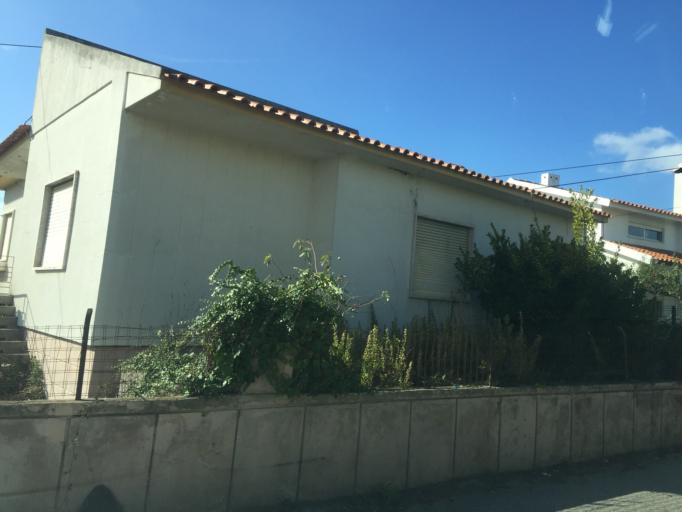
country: PT
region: Coimbra
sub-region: Figueira da Foz
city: Tavarede
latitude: 40.1624
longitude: -8.8431
